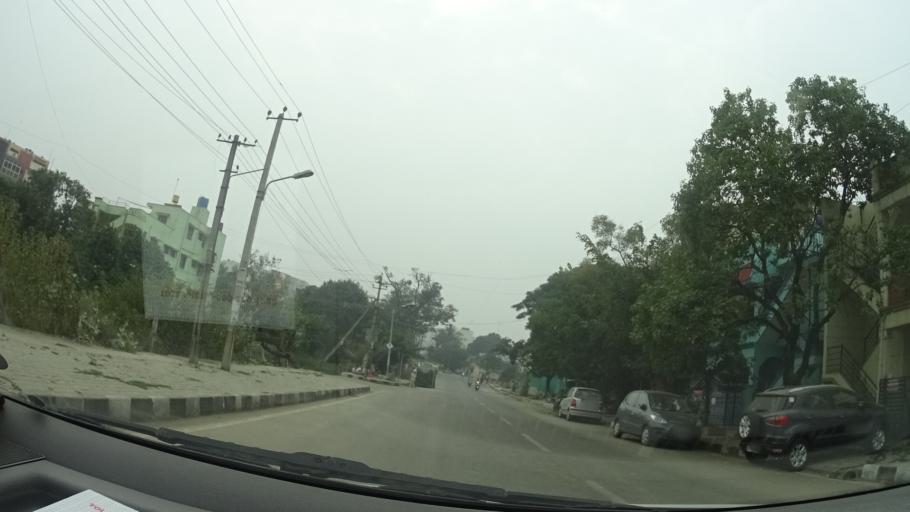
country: IN
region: Karnataka
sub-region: Bangalore Urban
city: Yelahanka
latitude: 13.0370
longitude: 77.6308
